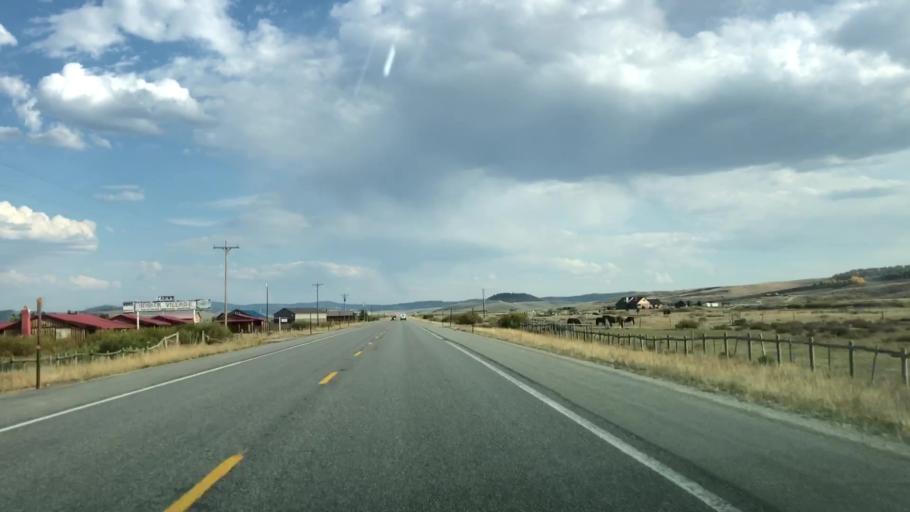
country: US
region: Wyoming
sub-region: Teton County
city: Hoback
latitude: 43.2045
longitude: -110.4104
